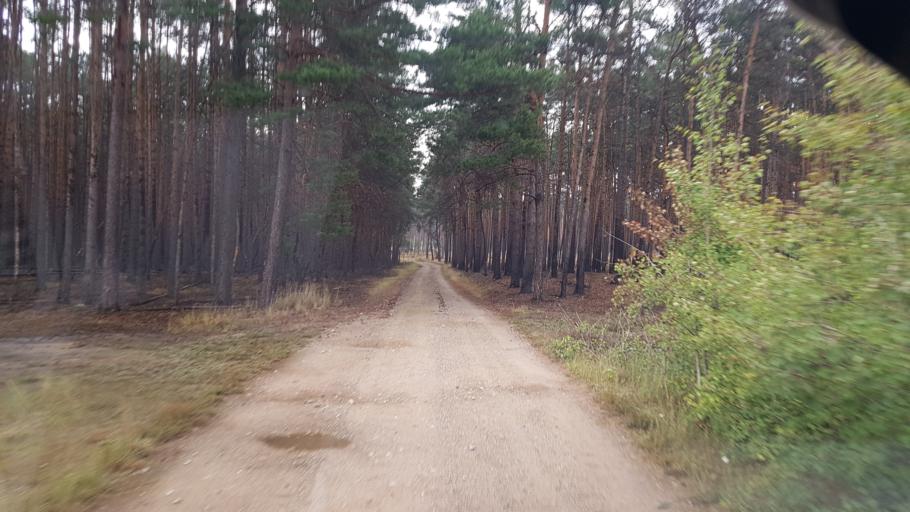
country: DE
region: Brandenburg
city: Finsterwalde
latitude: 51.6421
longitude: 13.7806
